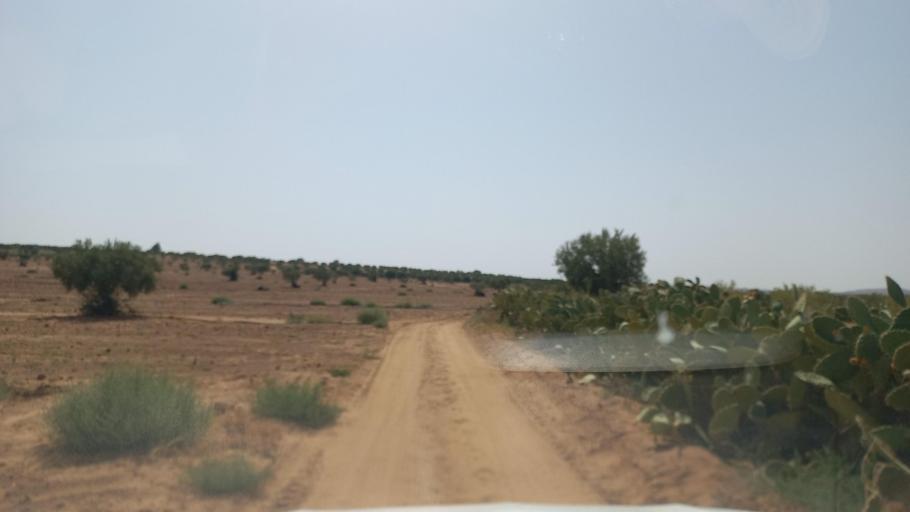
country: TN
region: Al Qasrayn
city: Kasserine
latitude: 35.2423
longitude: 9.0591
